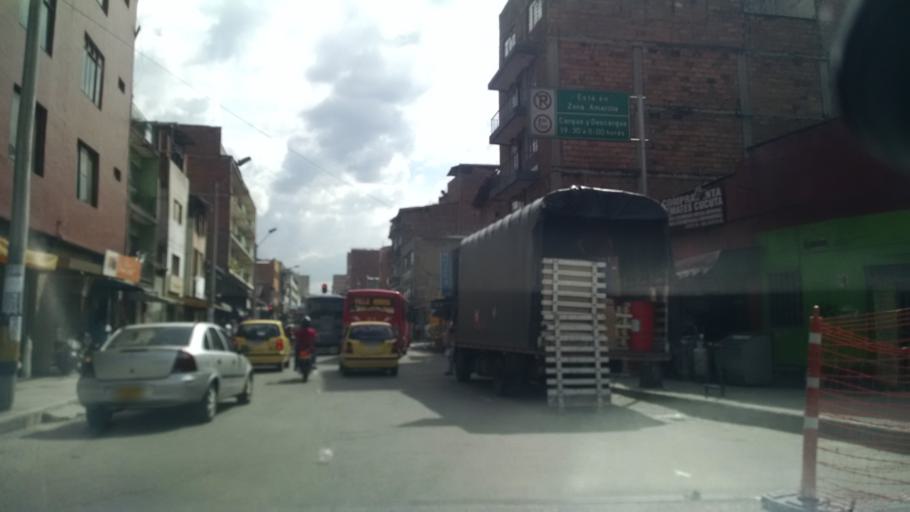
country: CO
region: Antioquia
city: Medellin
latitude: 6.2533
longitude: -75.5703
